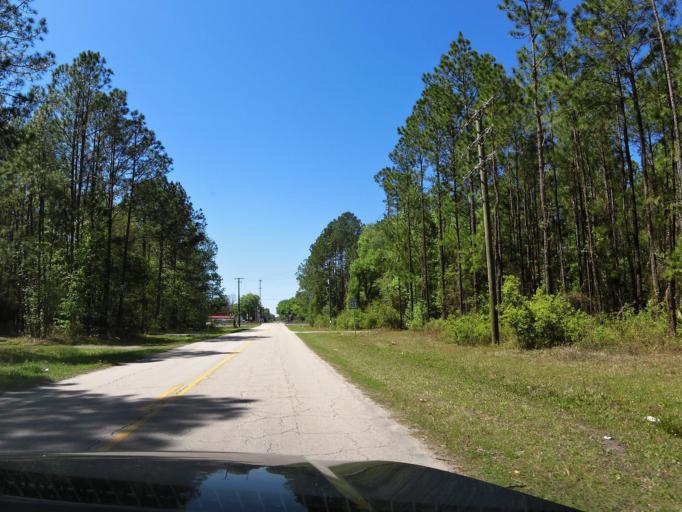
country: US
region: Florida
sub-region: Bradford County
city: Starke
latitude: 30.0559
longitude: -82.0653
